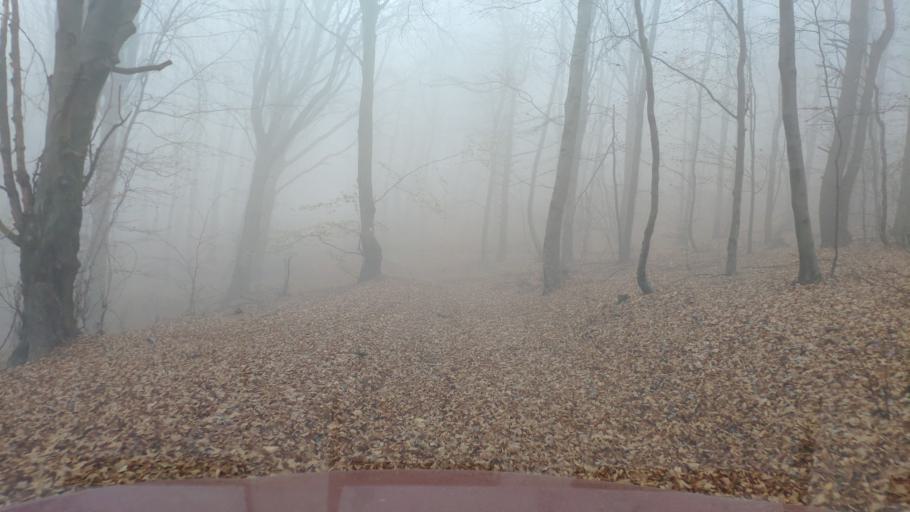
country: SK
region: Presovsky
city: Sabinov
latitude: 49.1520
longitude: 21.2275
